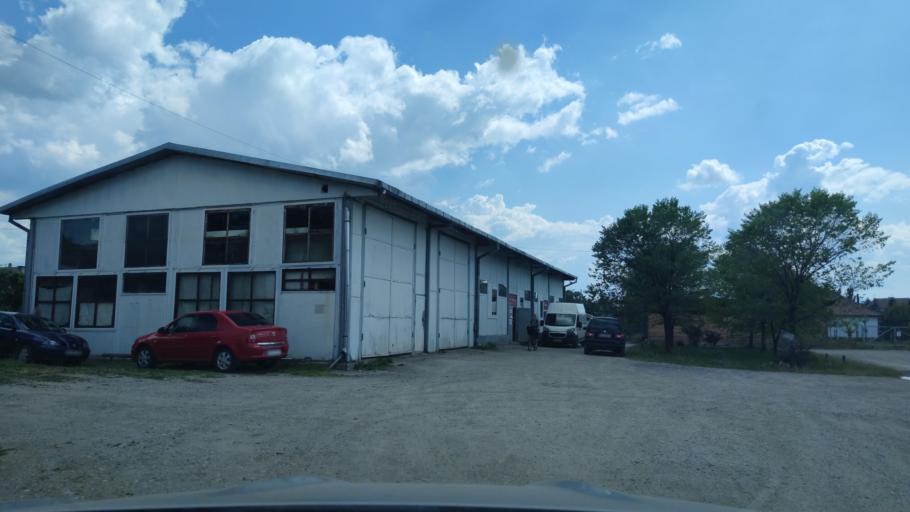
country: RO
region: Harghita
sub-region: Municipiul Gheorgheni
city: Gheorgheni
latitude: 46.7278
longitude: 25.6071
